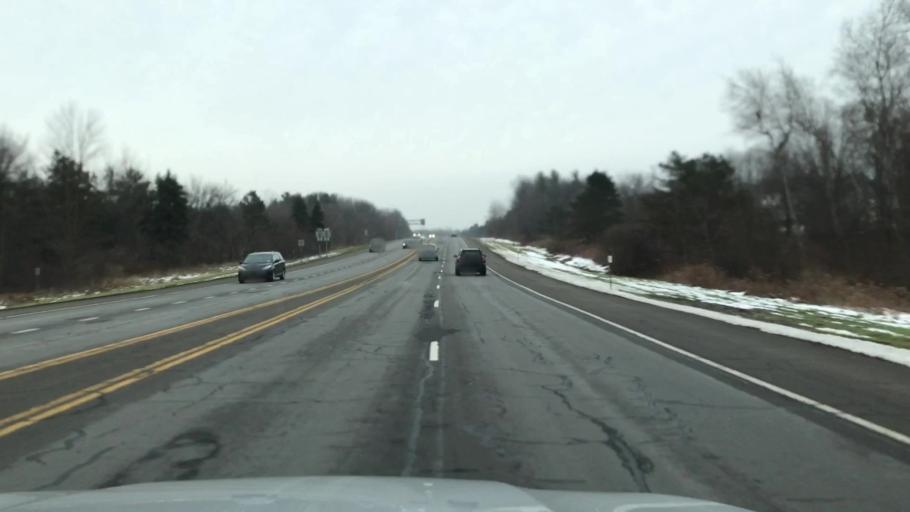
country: US
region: New York
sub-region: Erie County
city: Orchard Park
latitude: 42.7491
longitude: -78.7579
